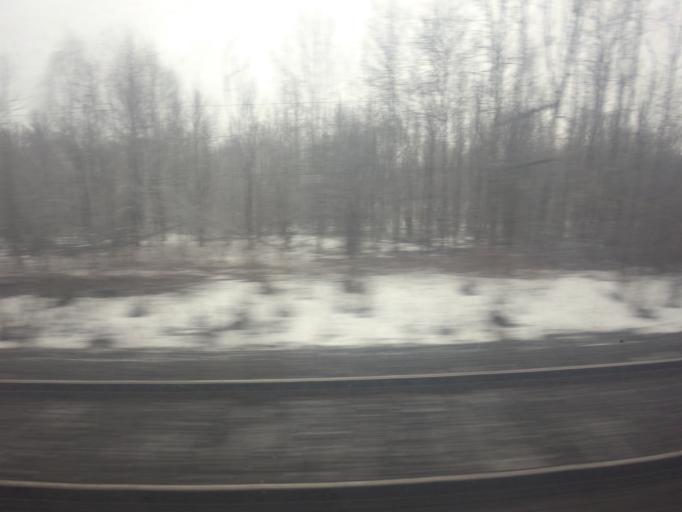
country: CA
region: Ontario
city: Brockville
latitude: 44.5719
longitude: -75.7542
